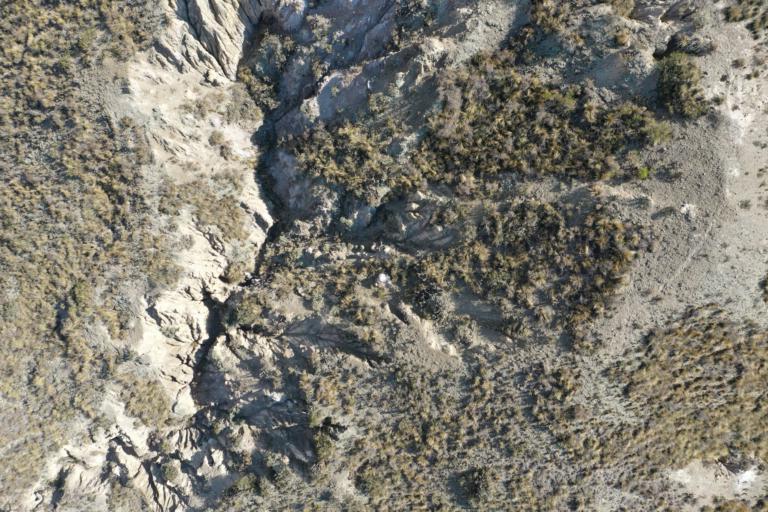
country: BO
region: La Paz
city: La Paz
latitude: -16.5606
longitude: -68.1233
